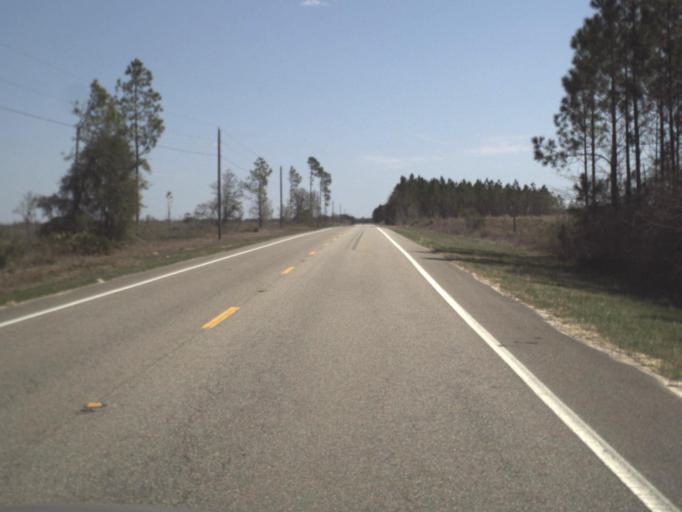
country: US
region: Florida
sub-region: Liberty County
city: Bristol
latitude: 30.5058
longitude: -84.8709
